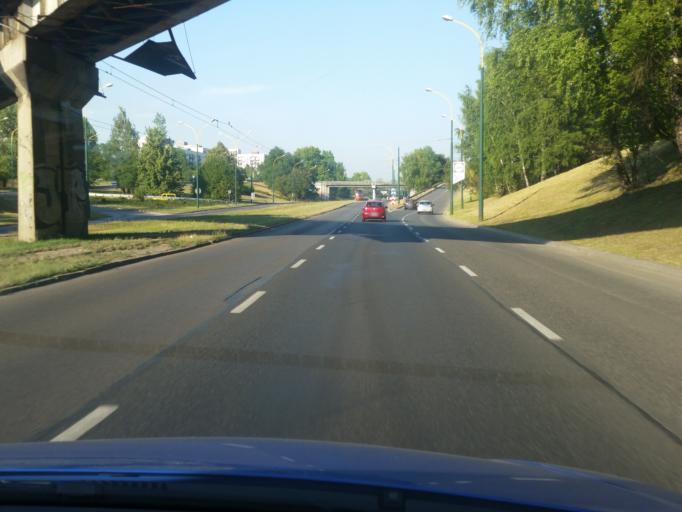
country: PL
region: Silesian Voivodeship
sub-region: Powiat bedzinski
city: Bedzin
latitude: 50.2888
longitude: 19.1542
